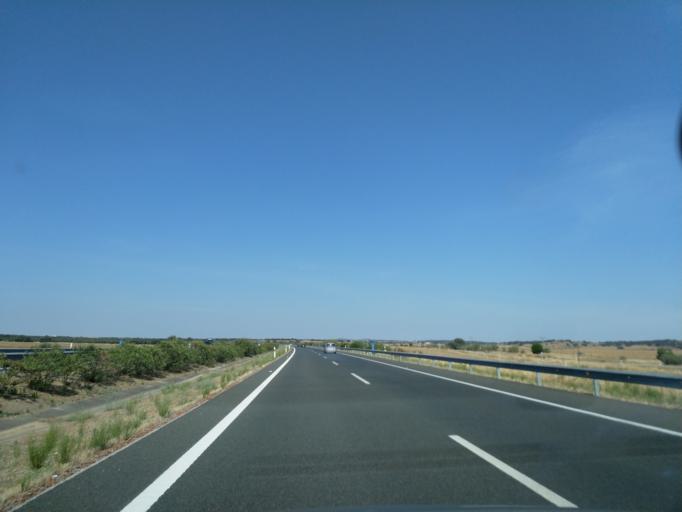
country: ES
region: Extremadura
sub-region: Provincia de Caceres
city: Casas de Don Antonio
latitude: 39.2521
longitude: -6.3088
